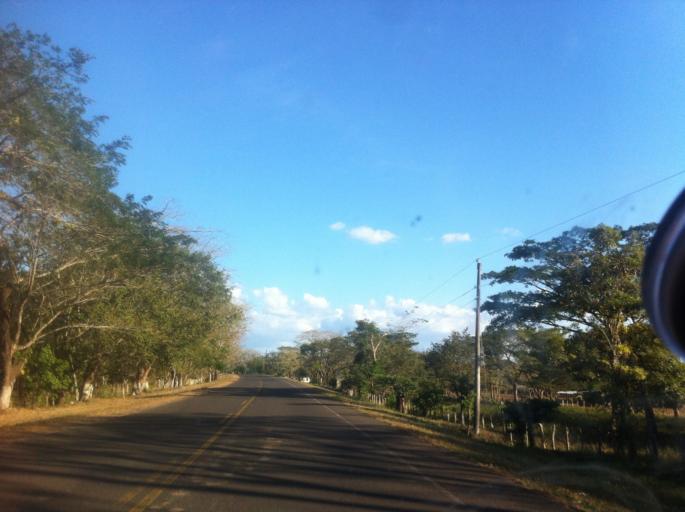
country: NI
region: Rio San Juan
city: Morrito
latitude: 11.7360
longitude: -84.9804
